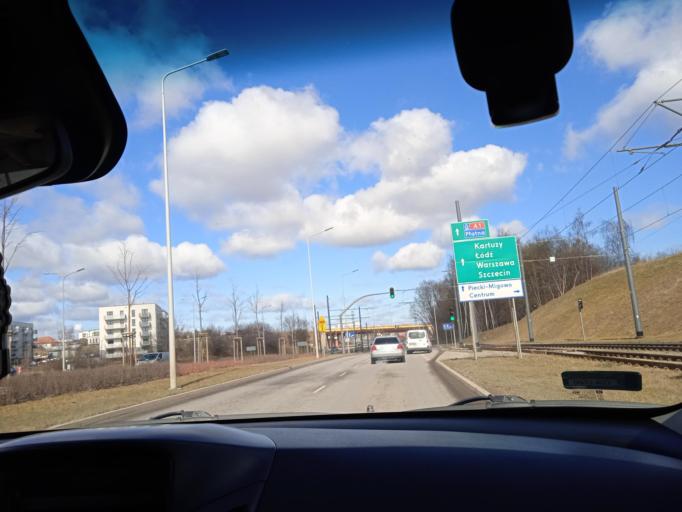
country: PL
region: Pomeranian Voivodeship
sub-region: Powiat gdanski
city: Kowale
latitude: 54.3324
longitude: 18.5702
